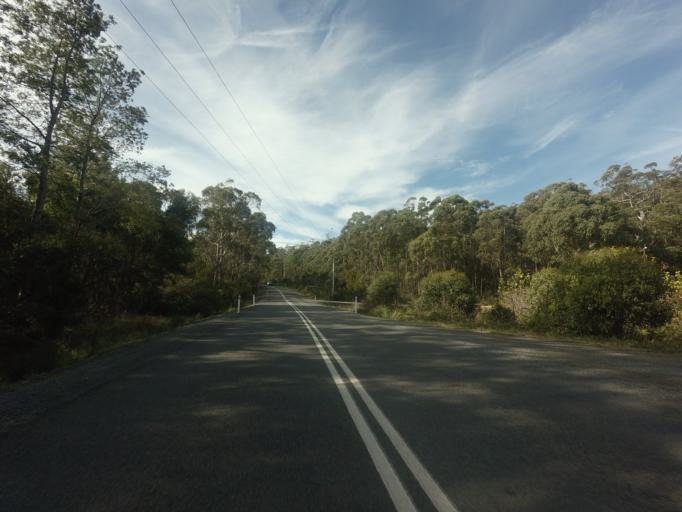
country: AU
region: Tasmania
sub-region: Clarence
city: Sandford
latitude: -43.0634
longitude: 147.8416
